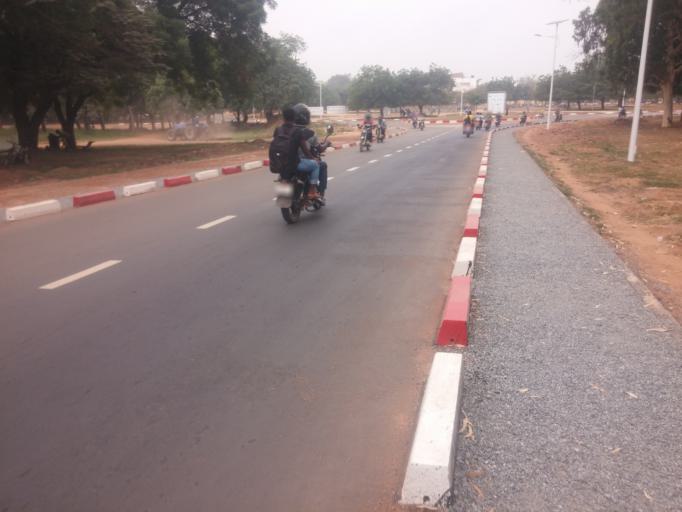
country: TG
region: Maritime
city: Lome
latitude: 6.1732
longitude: 1.2164
